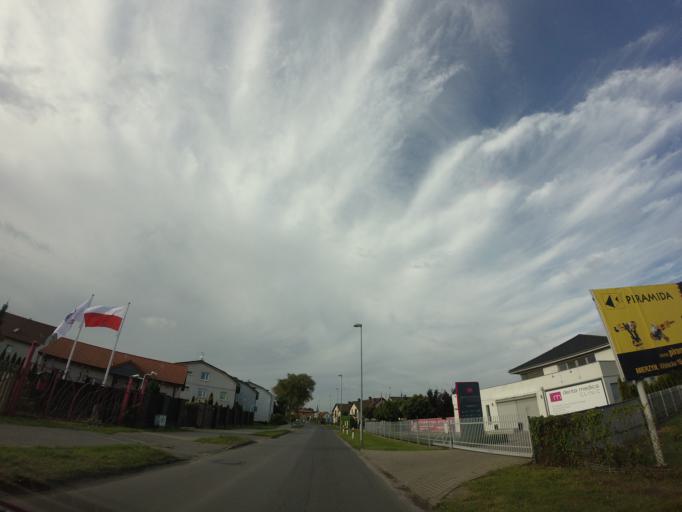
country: PL
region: West Pomeranian Voivodeship
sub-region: Powiat policki
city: Przeclaw
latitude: 53.4353
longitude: 14.4693
